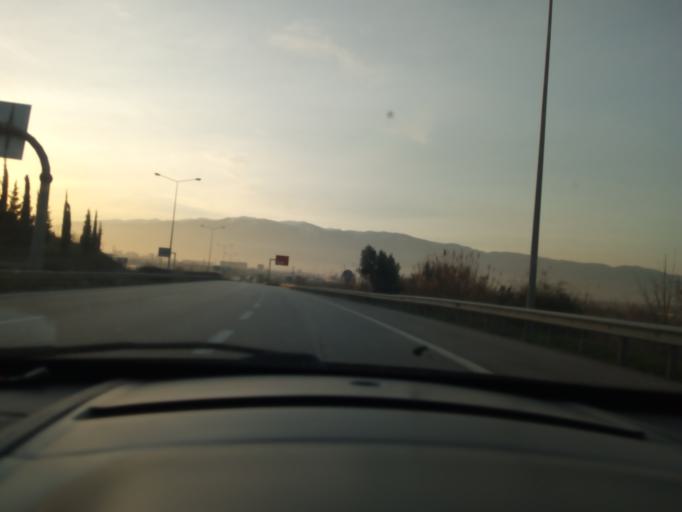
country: TR
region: Bursa
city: Demirtas
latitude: 40.2815
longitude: 29.0412
